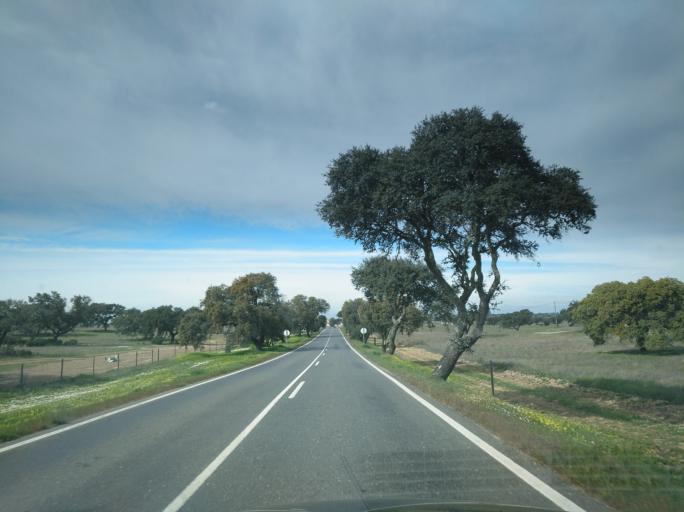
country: PT
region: Beja
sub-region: Mertola
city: Mertola
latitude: 37.7569
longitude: -7.8103
